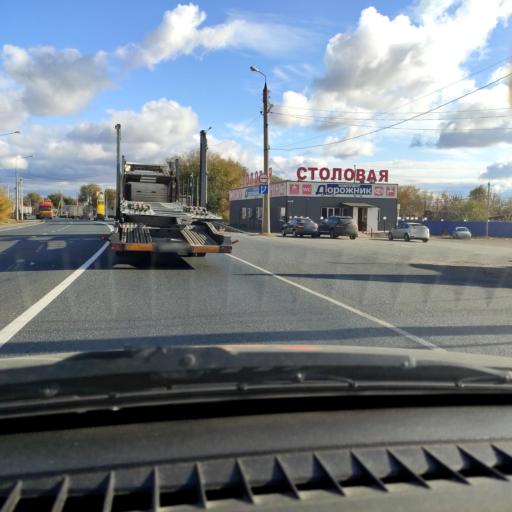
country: RU
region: Samara
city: Varlamovo
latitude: 53.1910
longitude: 48.3557
